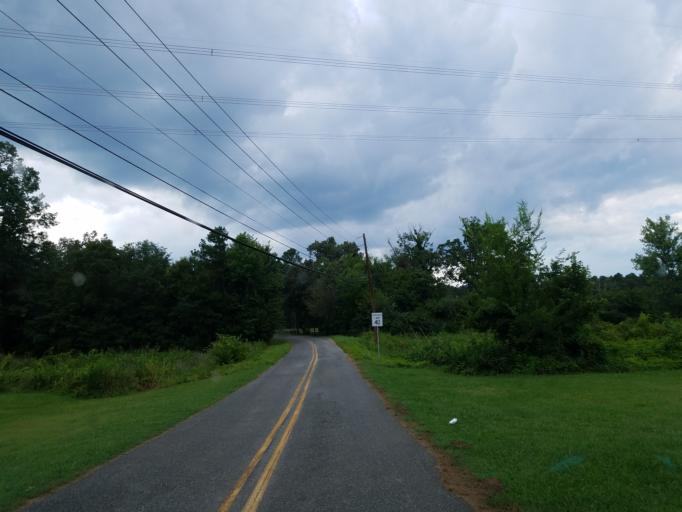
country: US
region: Georgia
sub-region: Floyd County
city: Shannon
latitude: 34.3869
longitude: -85.1785
